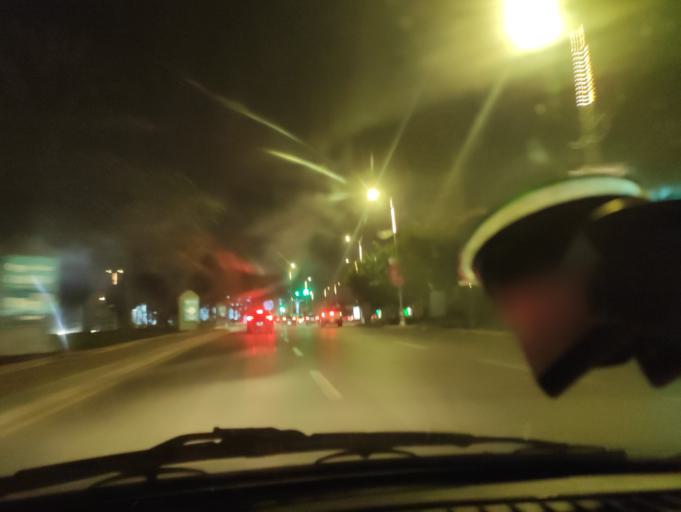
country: EG
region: Al Jizah
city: Awsim
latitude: 30.0213
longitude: 31.0060
